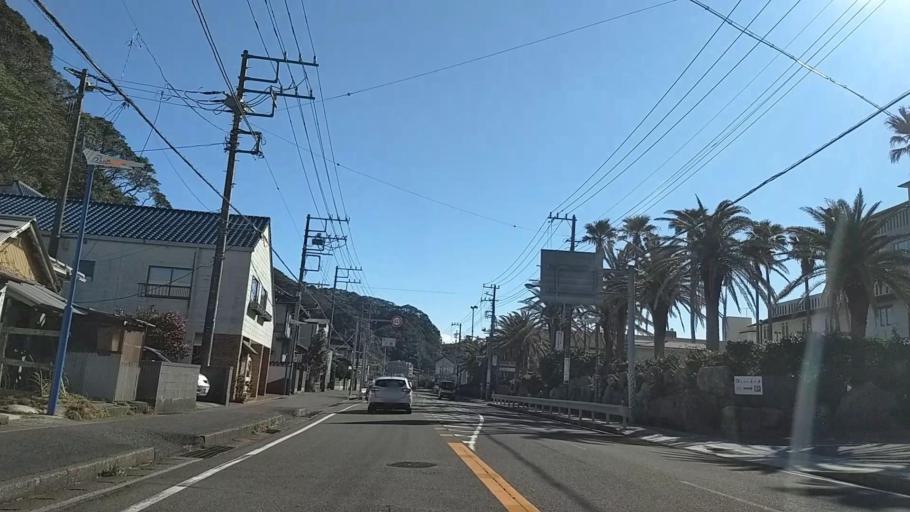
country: JP
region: Chiba
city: Kawaguchi
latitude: 35.1249
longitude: 140.1949
